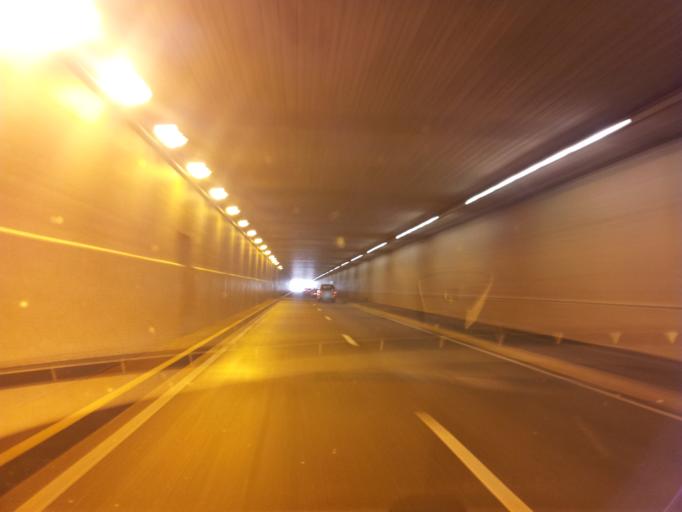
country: CH
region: Zurich
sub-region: Bezirk Dietikon
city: Dietikon / Vorstadt
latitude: 47.4183
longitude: 8.3900
